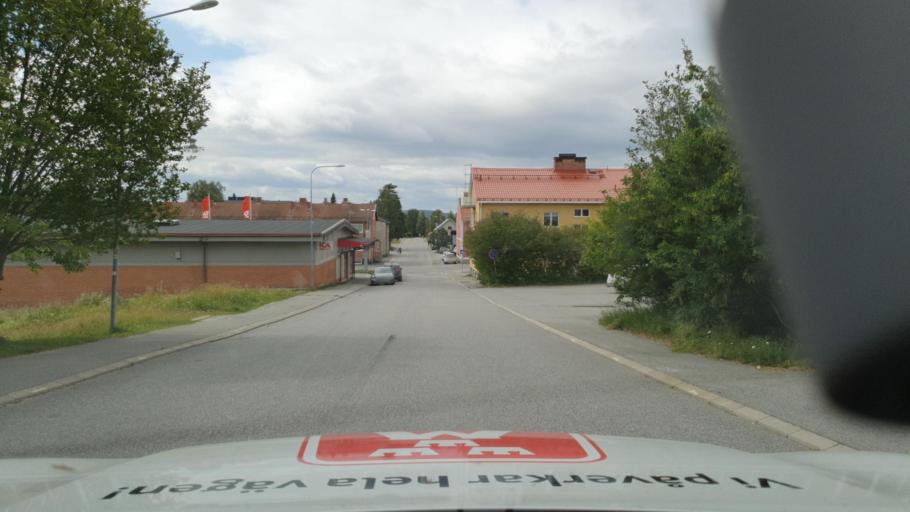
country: SE
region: Vaesterbotten
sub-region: Asele Kommun
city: Asele
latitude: 64.1610
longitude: 17.3554
